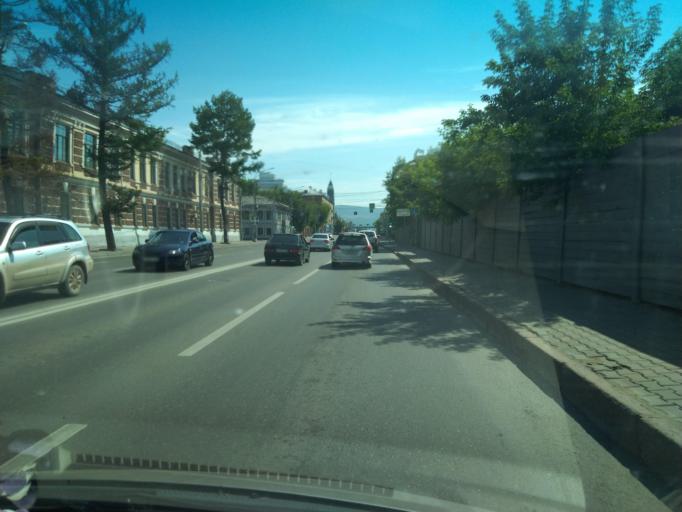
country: RU
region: Krasnoyarskiy
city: Krasnoyarsk
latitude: 56.0144
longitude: 92.8708
